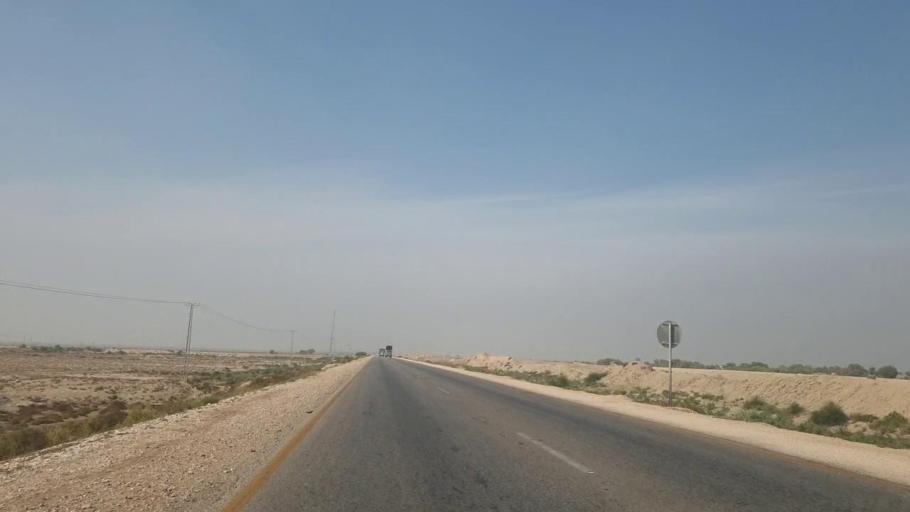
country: PK
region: Sindh
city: Sann
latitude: 25.9157
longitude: 68.2212
